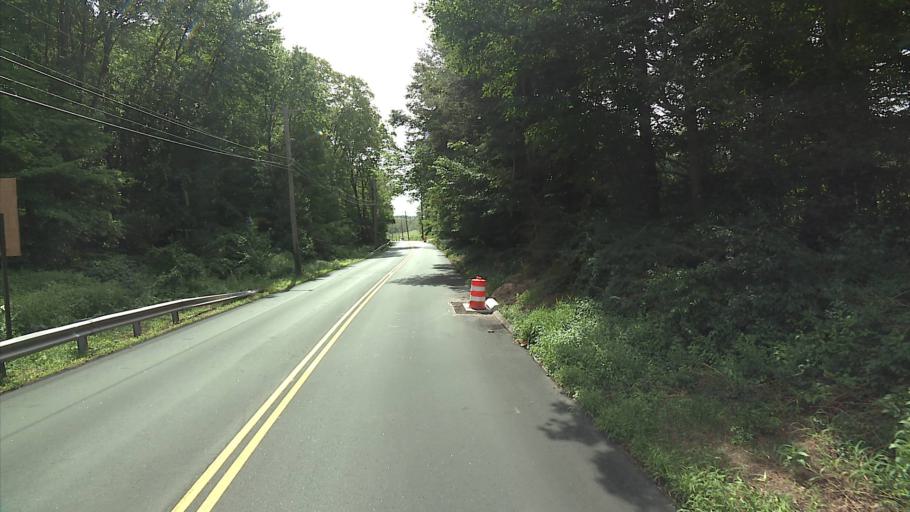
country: US
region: Connecticut
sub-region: Windham County
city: South Woodstock
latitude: 41.9489
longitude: -72.0110
